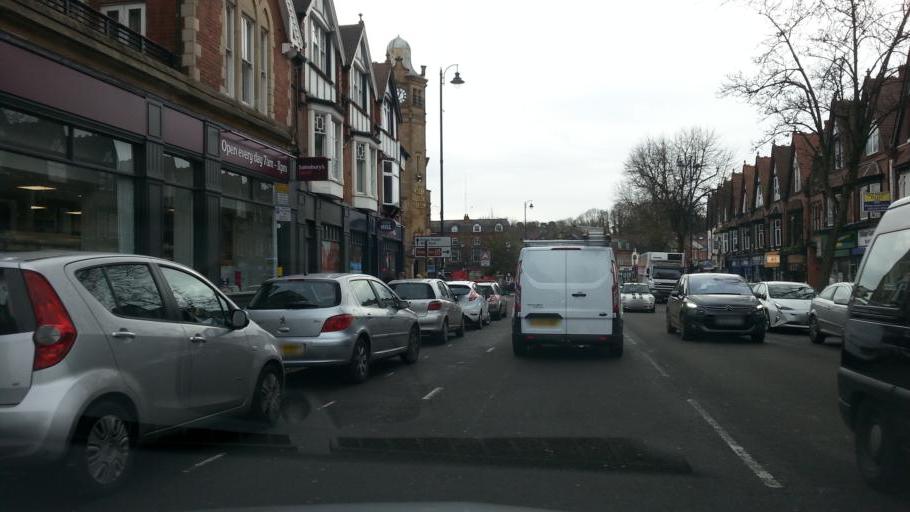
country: GB
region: England
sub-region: City and Borough of Birmingham
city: Birmingham
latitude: 52.4476
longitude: -1.8880
